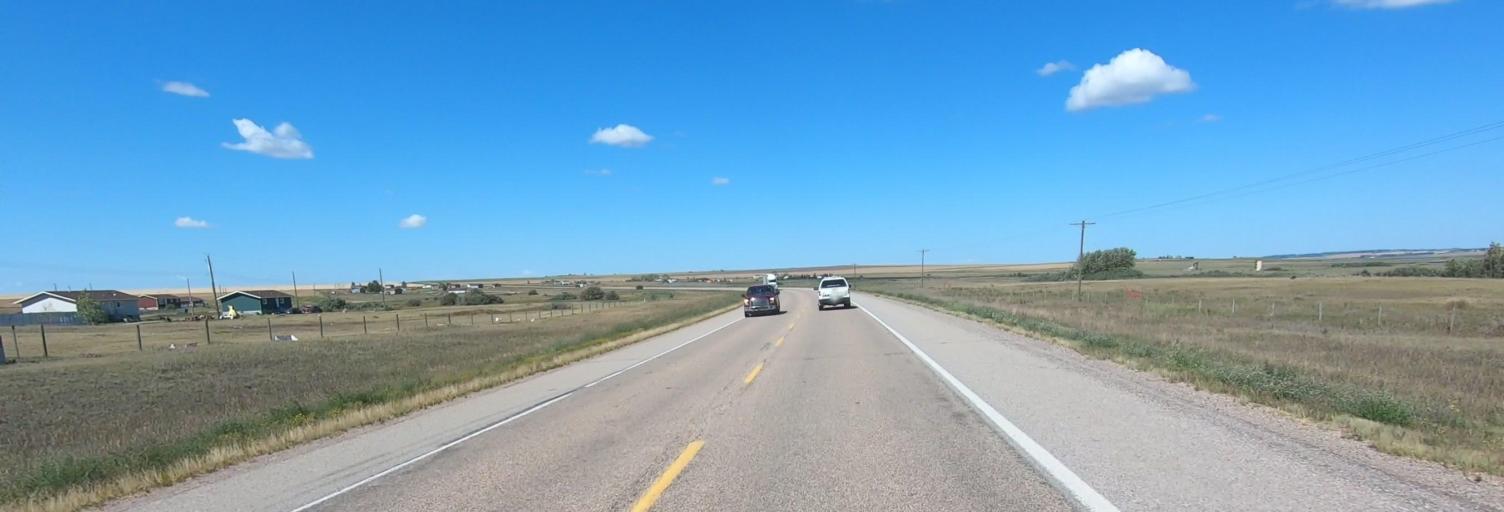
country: CA
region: Alberta
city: Strathmore
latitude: 50.8903
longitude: -113.1934
